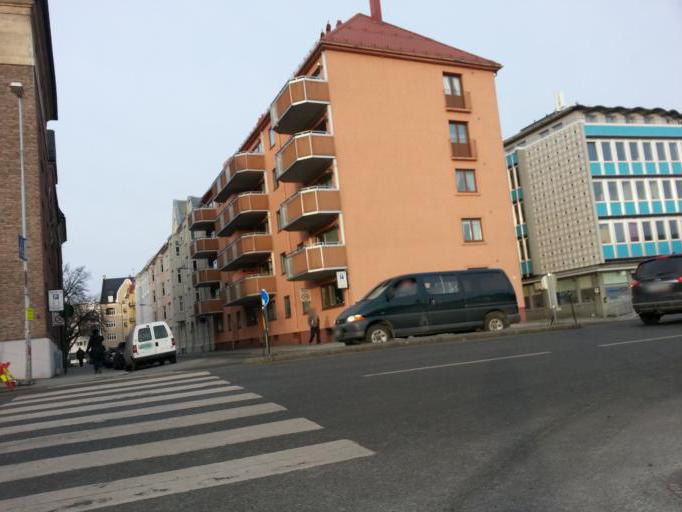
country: NO
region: Sor-Trondelag
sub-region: Trondheim
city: Trondheim
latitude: 63.4299
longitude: 10.3885
